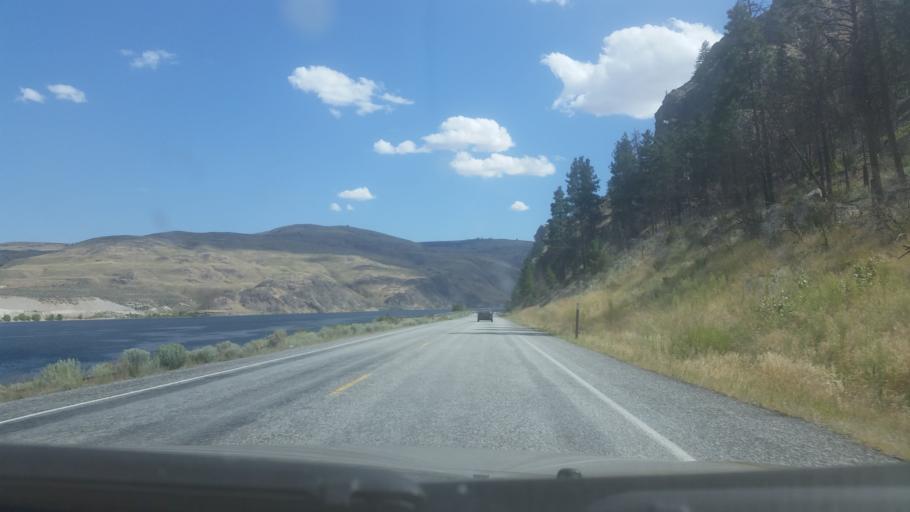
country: US
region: Washington
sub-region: Okanogan County
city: Brewster
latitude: 47.9657
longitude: -119.8811
